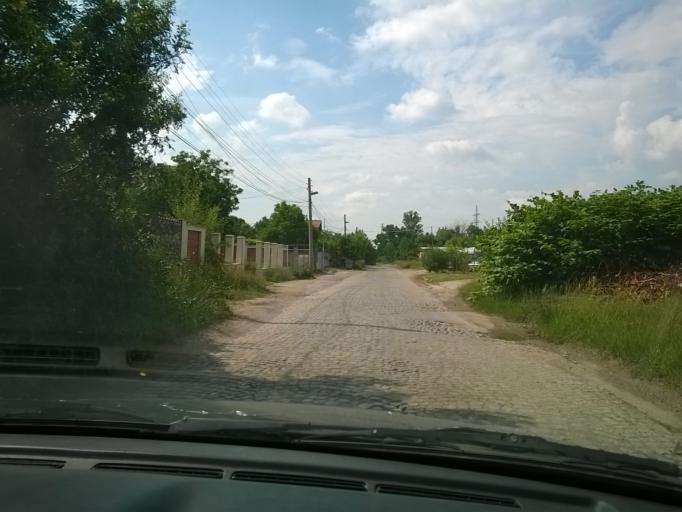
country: BG
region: Sofiya
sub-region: Obshtina Bozhurishte
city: Bozhurishte
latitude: 42.6842
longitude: 23.2362
